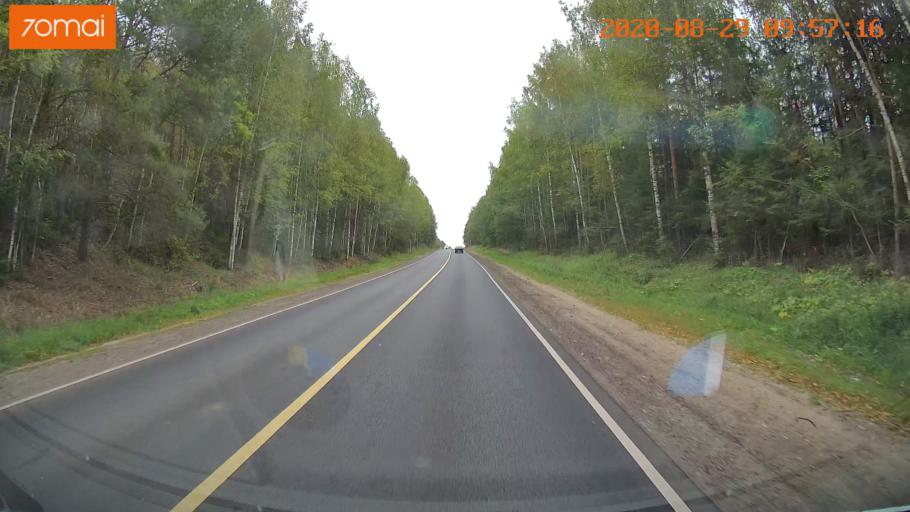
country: RU
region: Ivanovo
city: Zarechnyy
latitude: 57.4169
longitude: 42.3095
